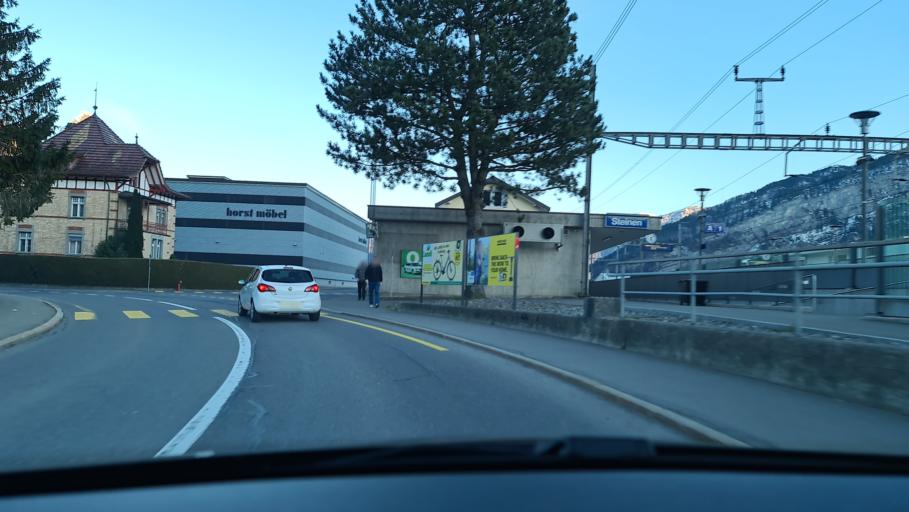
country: CH
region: Schwyz
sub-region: Bezirk Schwyz
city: Steinen
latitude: 47.0482
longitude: 8.6068
